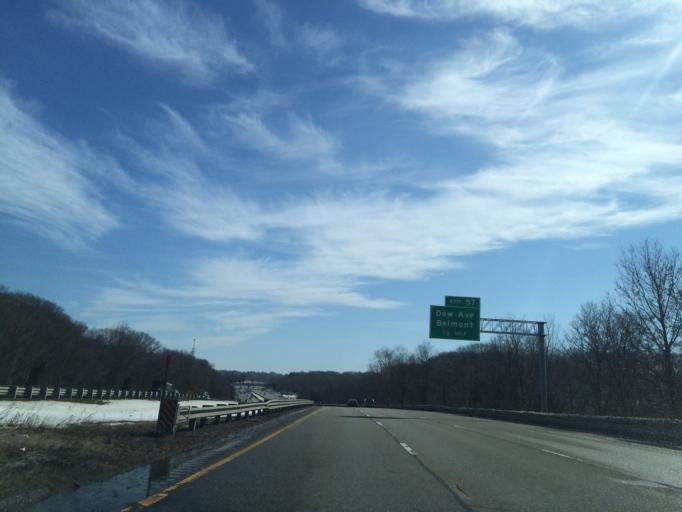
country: US
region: Massachusetts
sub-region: Middlesex County
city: Lexington
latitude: 42.4183
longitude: -71.2153
